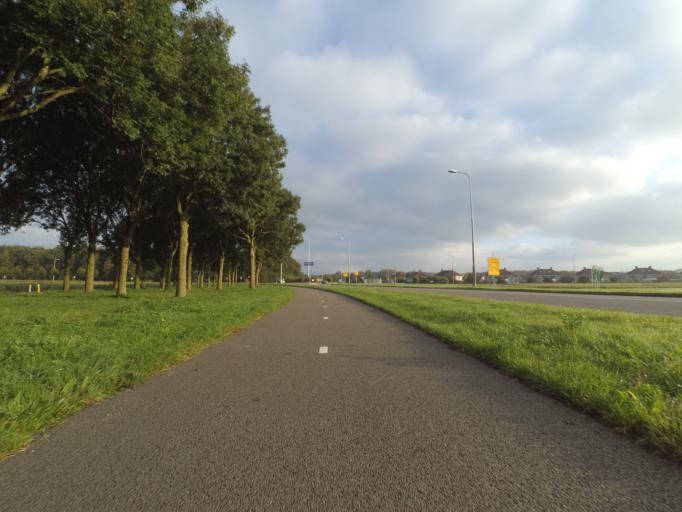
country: NL
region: Flevoland
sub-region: Gemeente Dronten
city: Dronten
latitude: 52.5156
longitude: 5.6894
